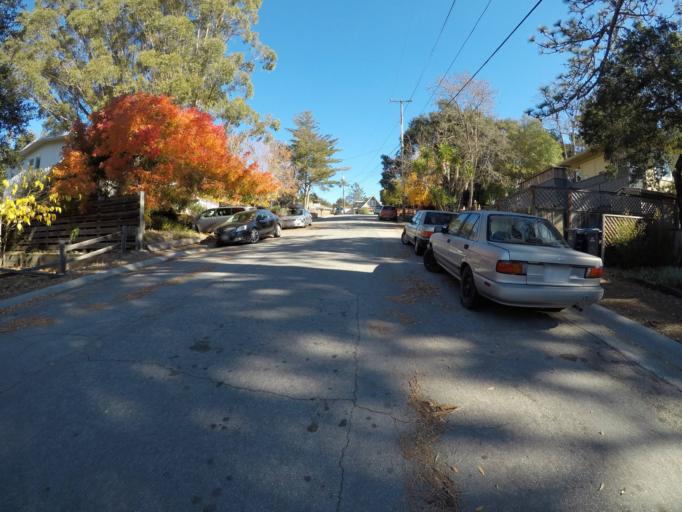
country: US
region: California
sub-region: Santa Cruz County
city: Scotts Valley
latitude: 37.0485
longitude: -122.0224
